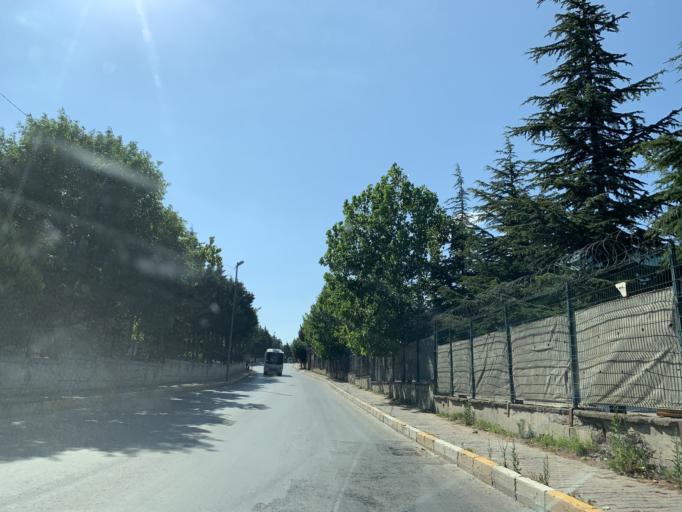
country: TR
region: Istanbul
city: Pendik
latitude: 40.8870
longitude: 29.2840
